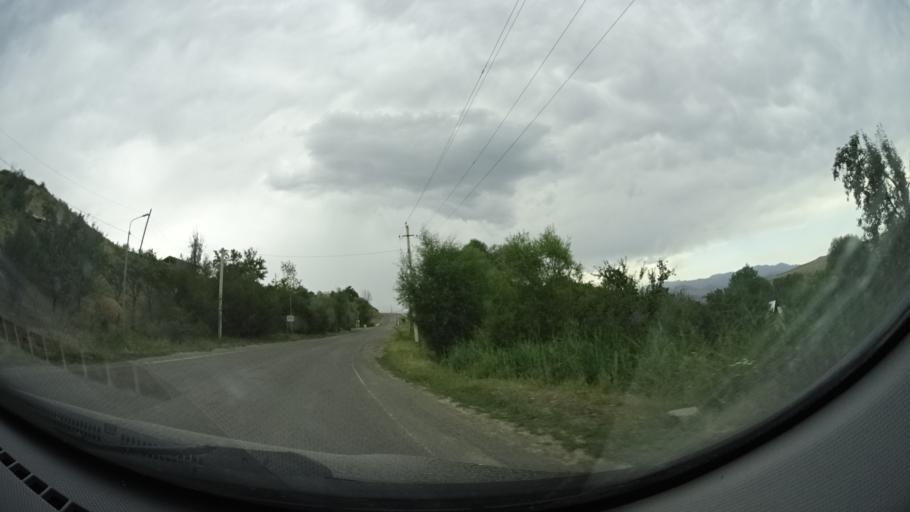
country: GE
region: Samtskhe-Javakheti
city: Akhaltsikhe
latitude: 41.6316
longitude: 43.0445
